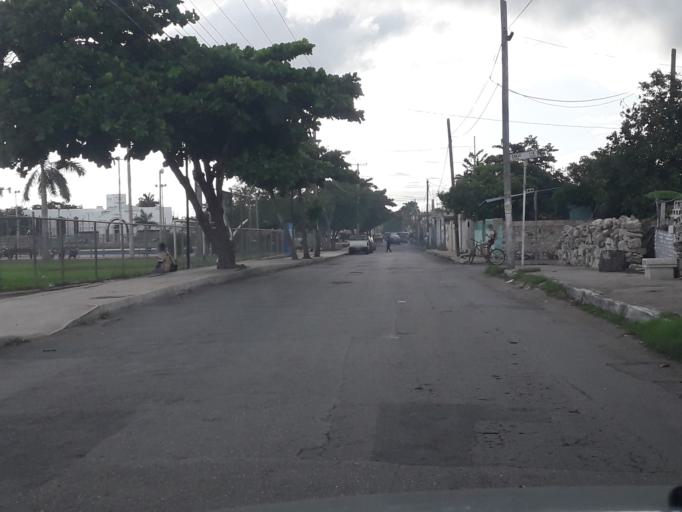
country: MX
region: Yucatan
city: Merida
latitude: 20.9608
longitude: -89.6586
